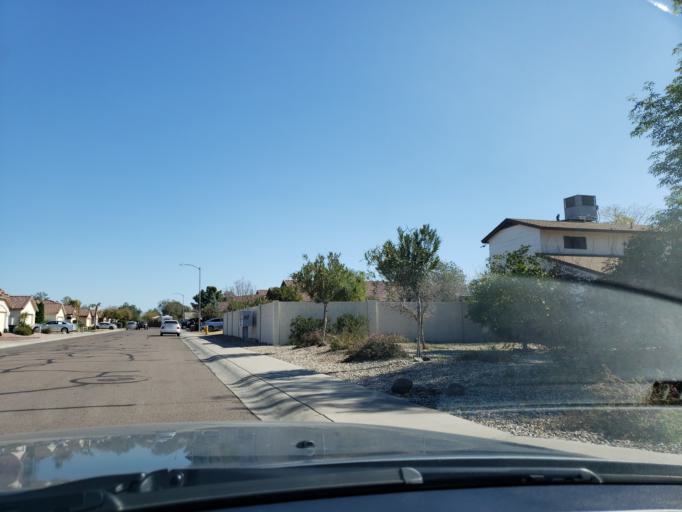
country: US
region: Arizona
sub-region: Maricopa County
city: Paradise Valley
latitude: 33.6427
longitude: -112.0395
